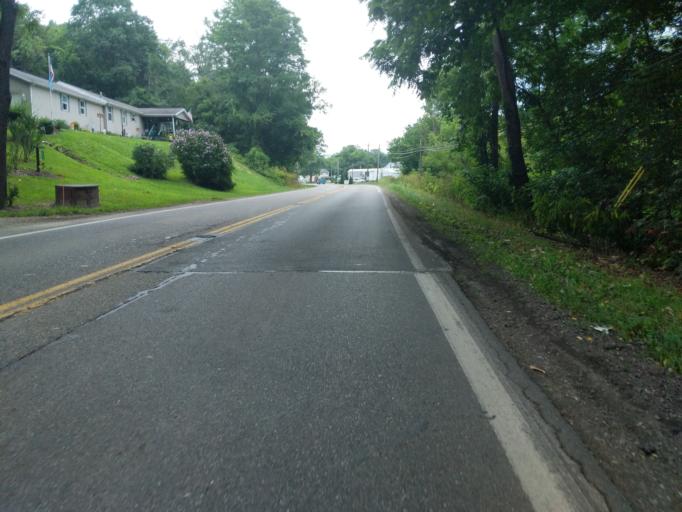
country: US
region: Ohio
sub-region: Athens County
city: Chauncey
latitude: 39.3941
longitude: -82.1395
